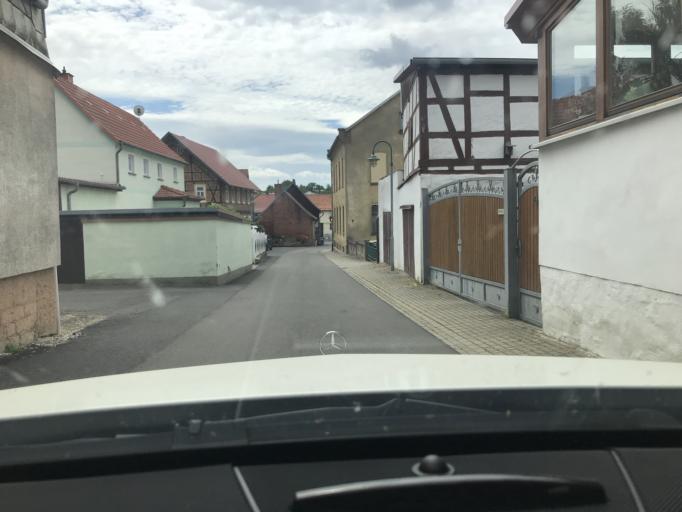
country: DE
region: Thuringia
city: Holzsussra
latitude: 51.2940
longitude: 10.6942
